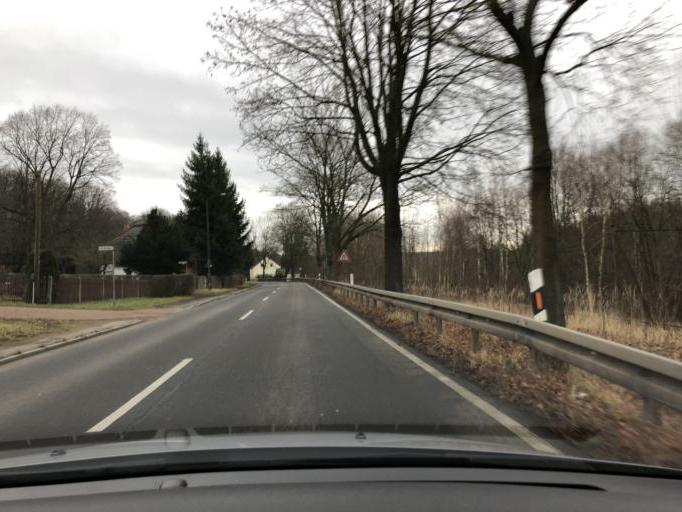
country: DE
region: Saxony
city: Niederstriegis
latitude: 51.0751
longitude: 13.1577
